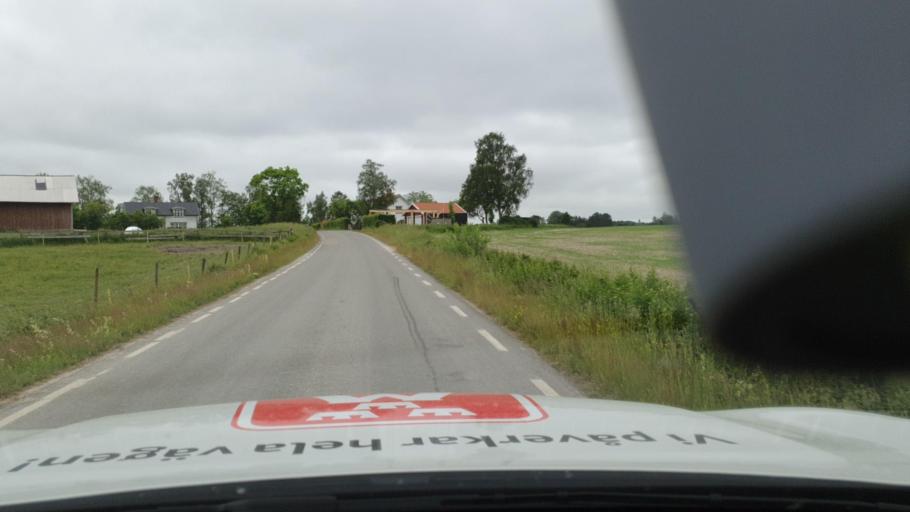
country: SE
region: Vaestra Goetaland
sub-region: Tibro Kommun
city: Tibro
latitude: 58.3960
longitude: 14.1178
